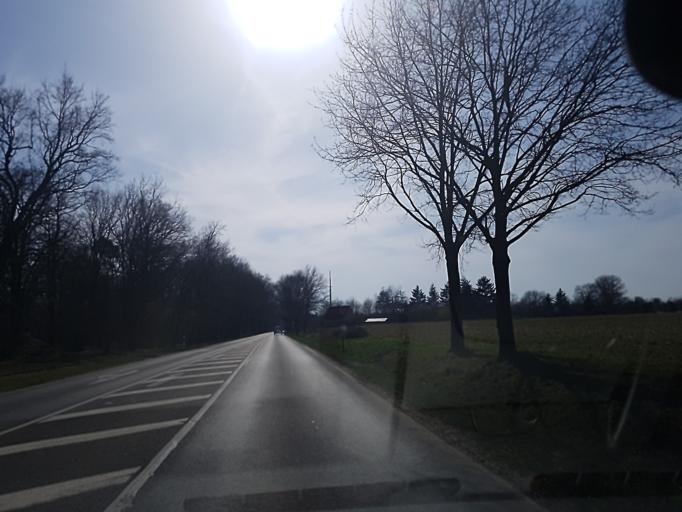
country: DE
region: Brandenburg
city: Calau
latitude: 51.7513
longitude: 13.9646
